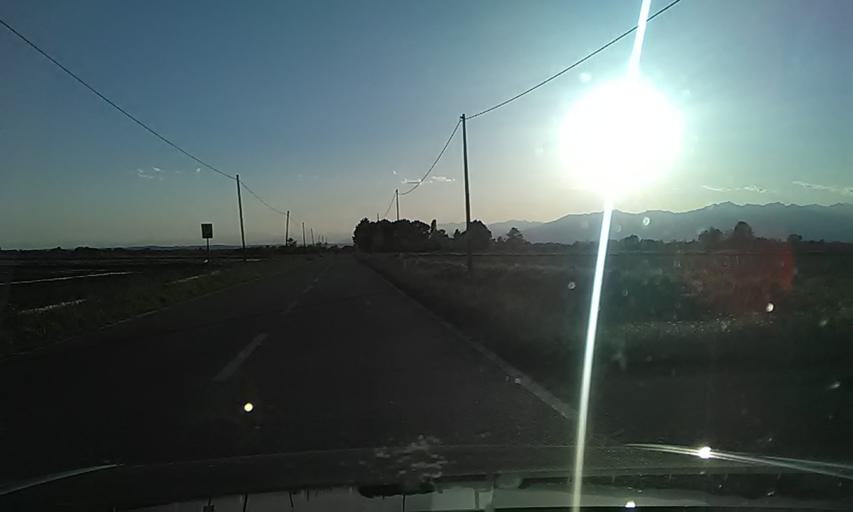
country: IT
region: Piedmont
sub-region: Provincia di Vercelli
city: Ghislarengo
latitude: 45.5226
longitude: 8.3556
